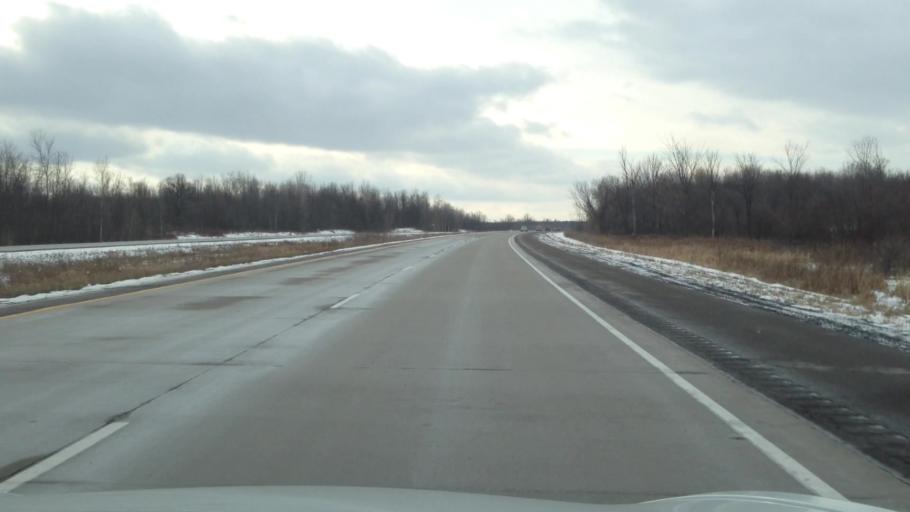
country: CA
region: Ontario
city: Hawkesbury
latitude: 45.3967
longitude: -74.7772
